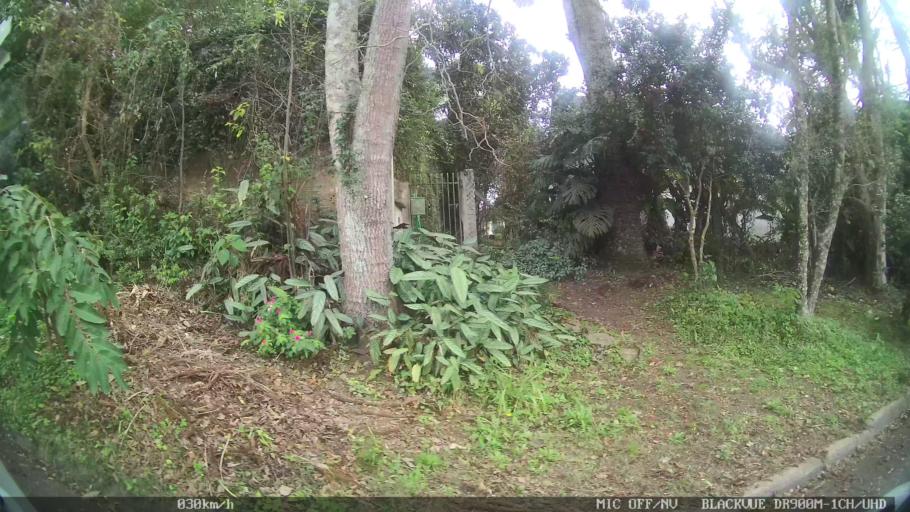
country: BR
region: Parana
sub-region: Curitiba
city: Curitiba
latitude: -25.3706
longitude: -49.2557
